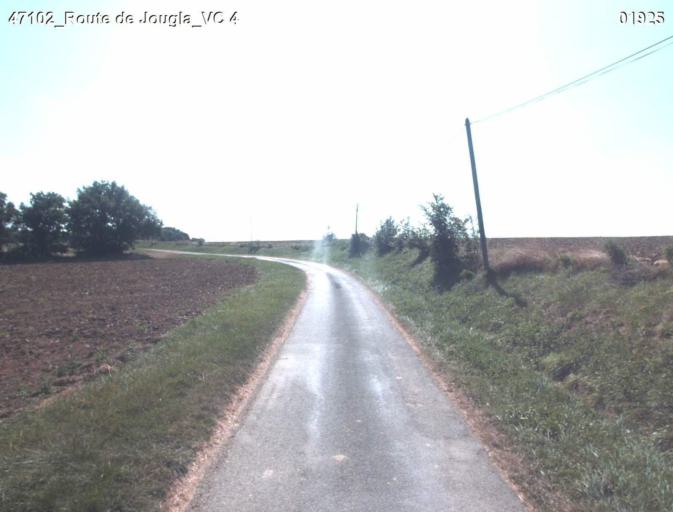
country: FR
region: Aquitaine
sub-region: Departement du Lot-et-Garonne
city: Laplume
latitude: 44.0580
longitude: 0.4326
